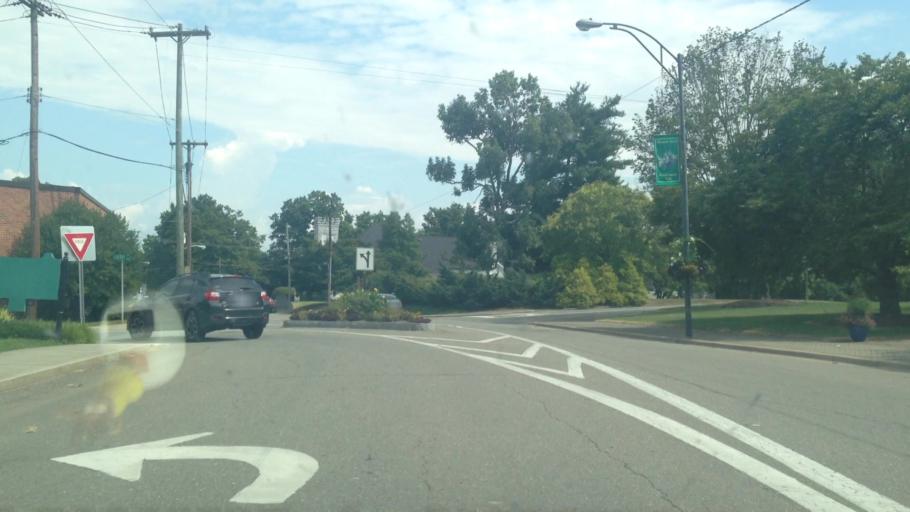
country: US
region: North Carolina
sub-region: Surry County
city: Mount Airy
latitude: 36.4983
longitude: -80.6065
